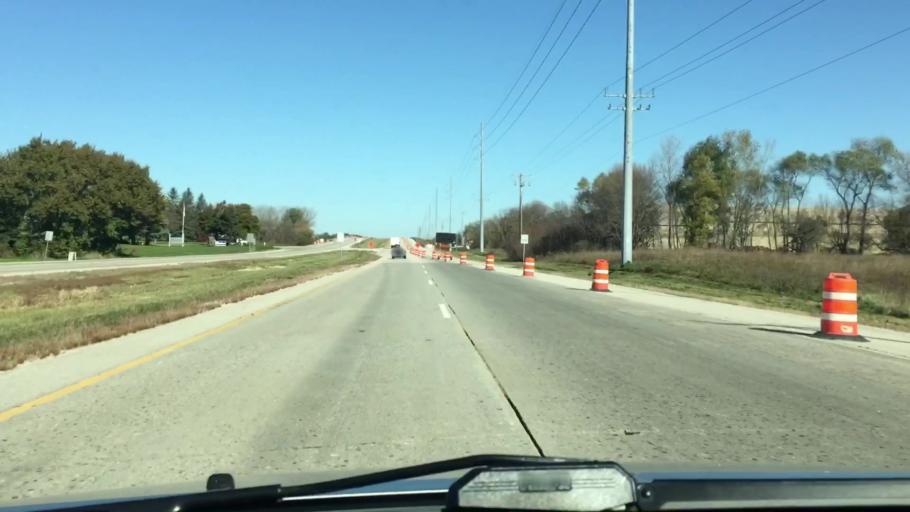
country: US
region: Wisconsin
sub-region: Waukesha County
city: Pewaukee
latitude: 43.0672
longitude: -88.2056
